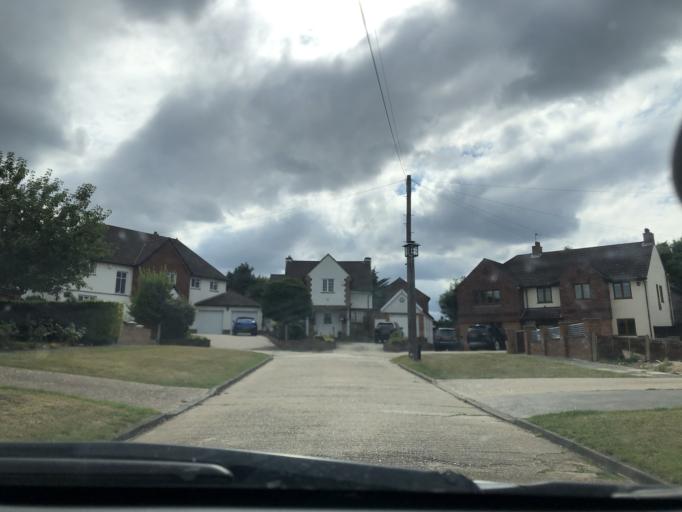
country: GB
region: England
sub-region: Kent
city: Dartford
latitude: 51.4285
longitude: 0.2063
